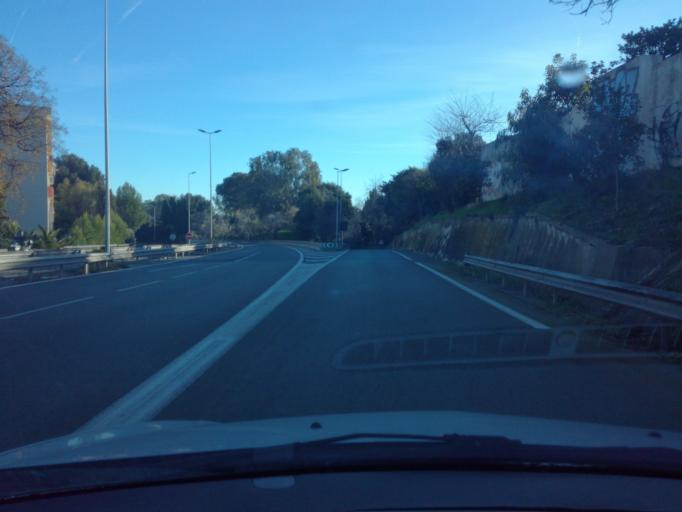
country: FR
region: Provence-Alpes-Cote d'Azur
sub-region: Departement des Alpes-Maritimes
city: Antibes
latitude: 43.5800
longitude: 7.1129
